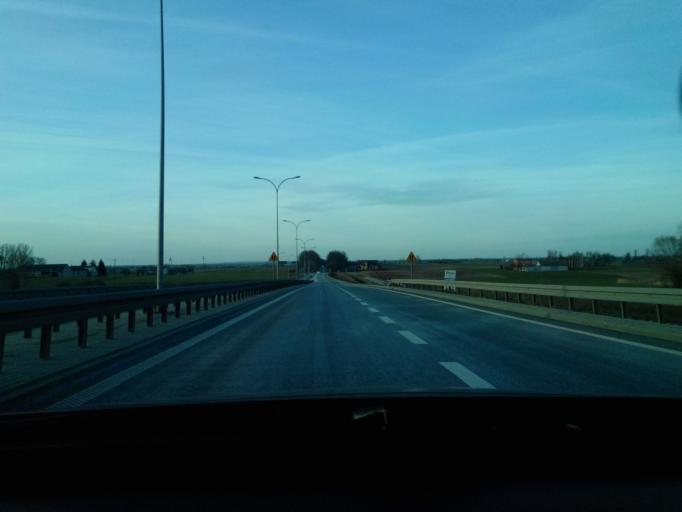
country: PL
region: Kujawsko-Pomorskie
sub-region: Powiat wloclawski
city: Kowal
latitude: 52.4859
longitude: 19.1537
